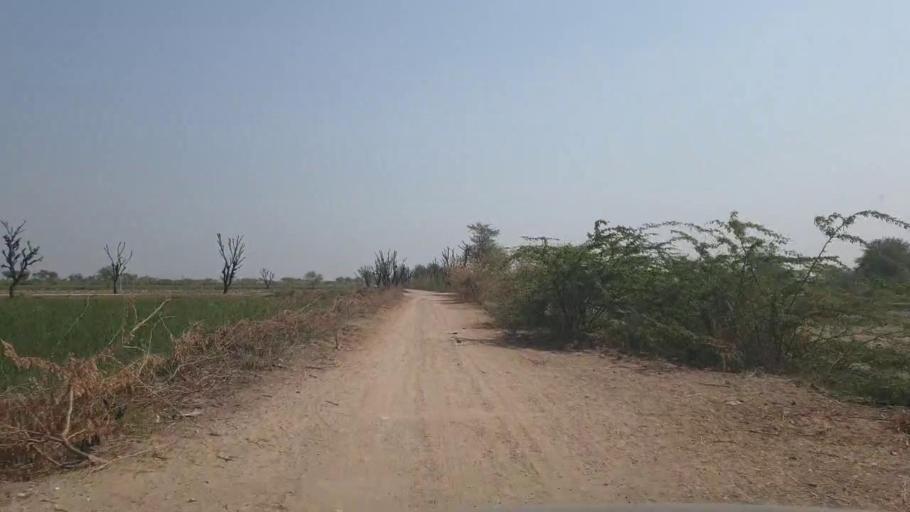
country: PK
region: Sindh
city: Dhoro Naro
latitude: 25.4861
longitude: 69.5423
